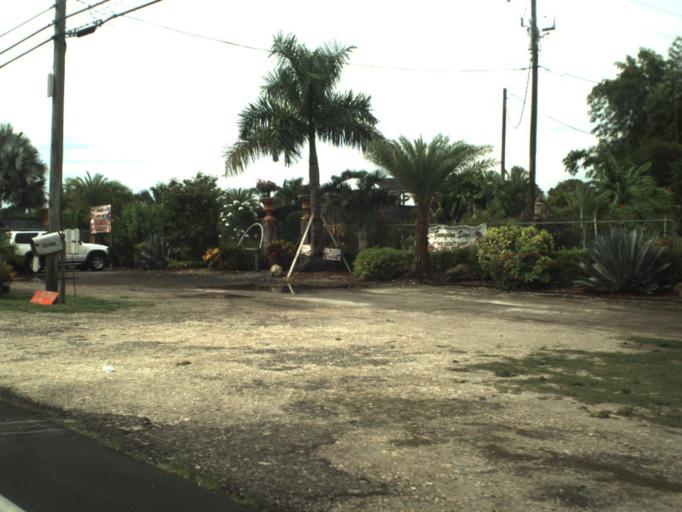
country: US
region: Florida
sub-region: Miami-Dade County
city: Richmond West
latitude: 25.5766
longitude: -80.4784
